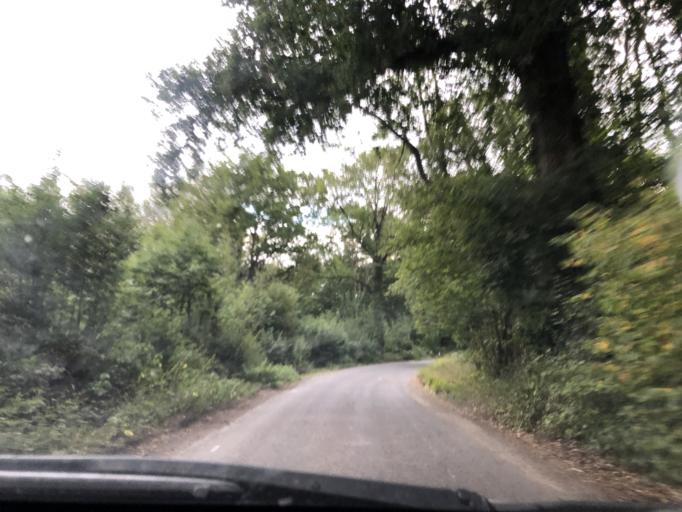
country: GB
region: England
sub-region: Kent
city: Sevenoaks
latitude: 51.2385
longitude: 0.2209
